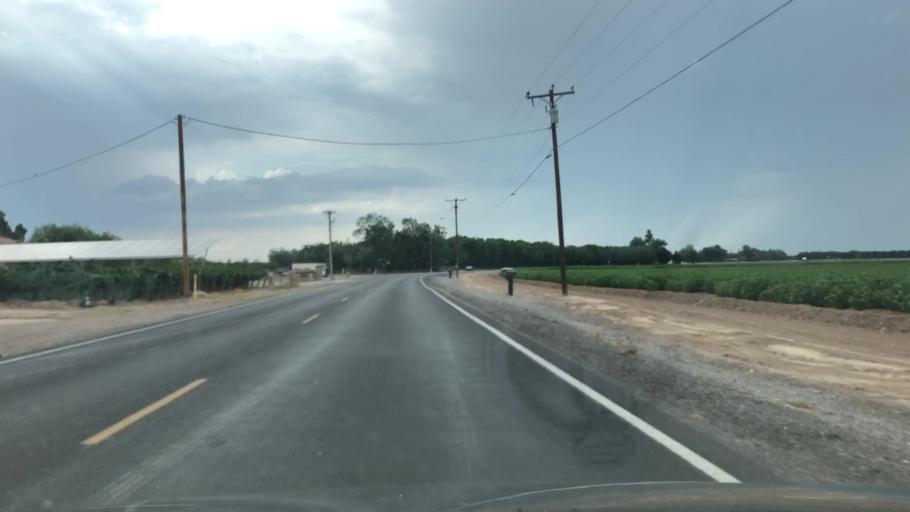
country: US
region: New Mexico
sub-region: Dona Ana County
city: La Union
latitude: 31.9688
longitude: -106.6509
